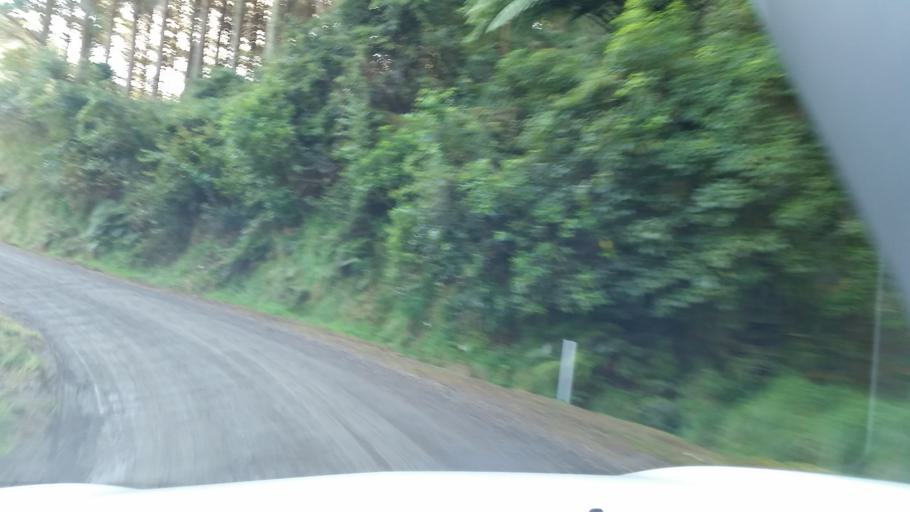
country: NZ
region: Taranaki
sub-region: South Taranaki District
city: Eltham
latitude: -39.5059
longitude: 174.3997
